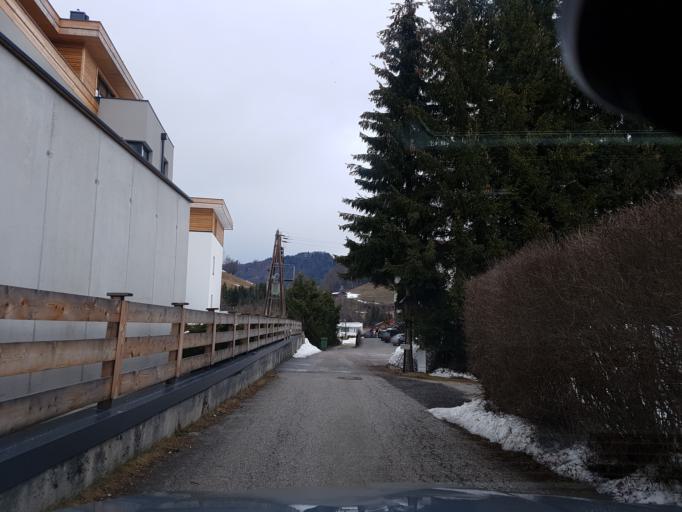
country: AT
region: Tyrol
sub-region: Politischer Bezirk Kufstein
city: Worgl
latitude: 47.4509
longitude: 12.0891
